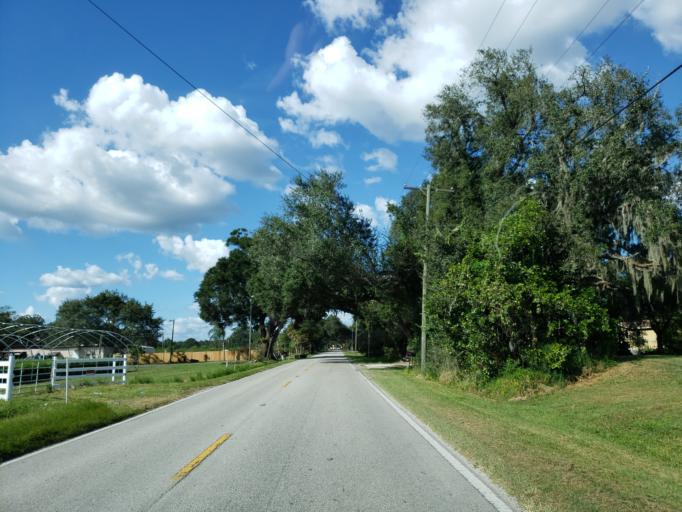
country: US
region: Florida
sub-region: Hillsborough County
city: Dover
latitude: 27.9887
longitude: -82.1869
